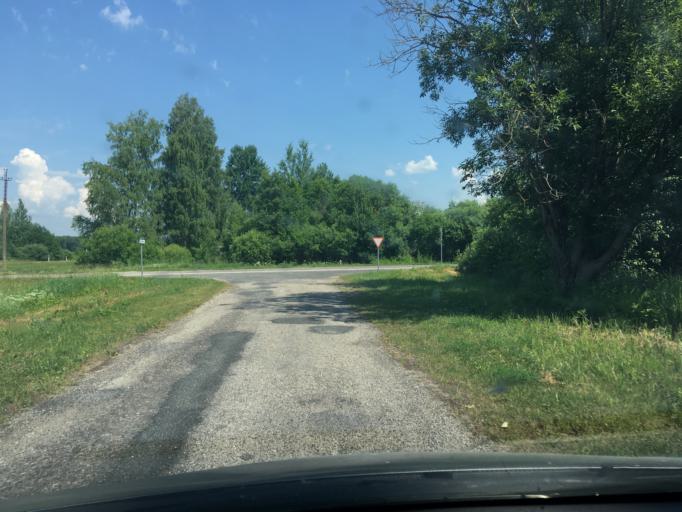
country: EE
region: Laeaene
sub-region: Lihula vald
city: Lihula
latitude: 58.6683
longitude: 23.7658
